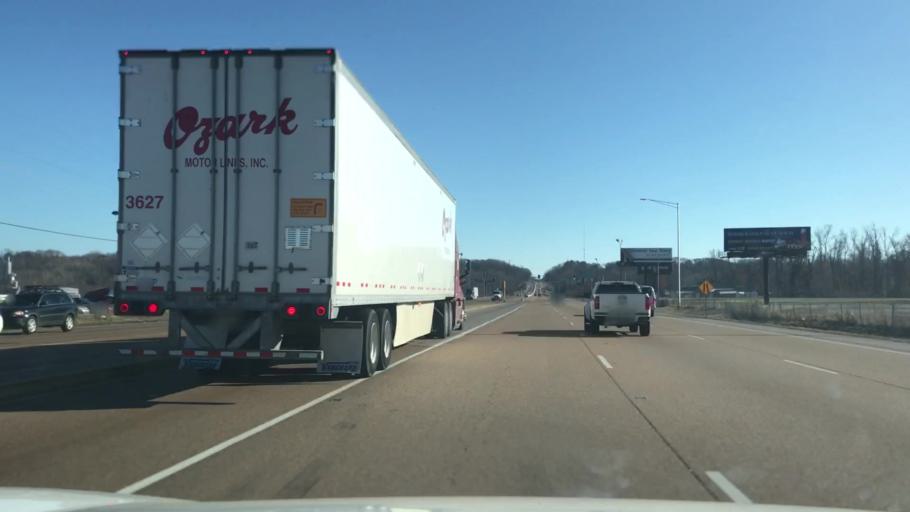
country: US
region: Illinois
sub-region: Saint Clair County
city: Alorton
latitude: 38.5757
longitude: -90.1003
